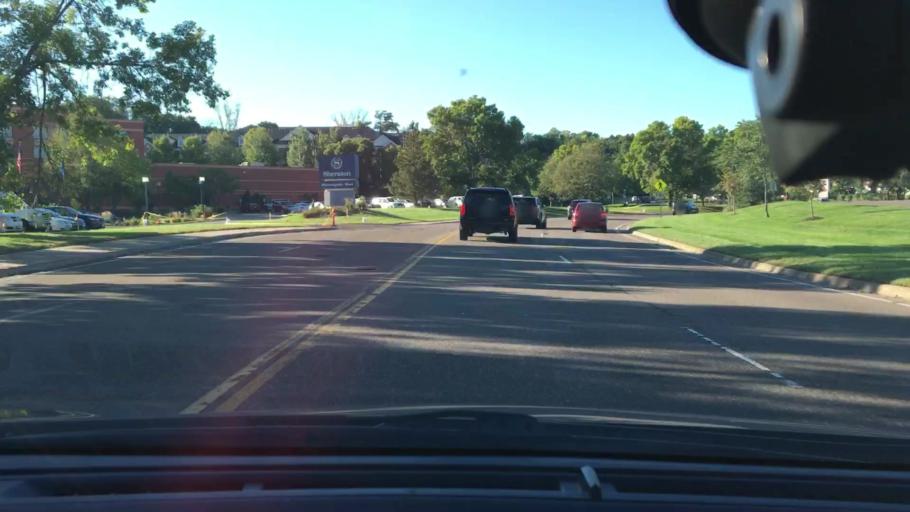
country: US
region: Minnesota
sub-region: Hennepin County
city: Minnetonka Mills
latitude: 44.9674
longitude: -93.4330
